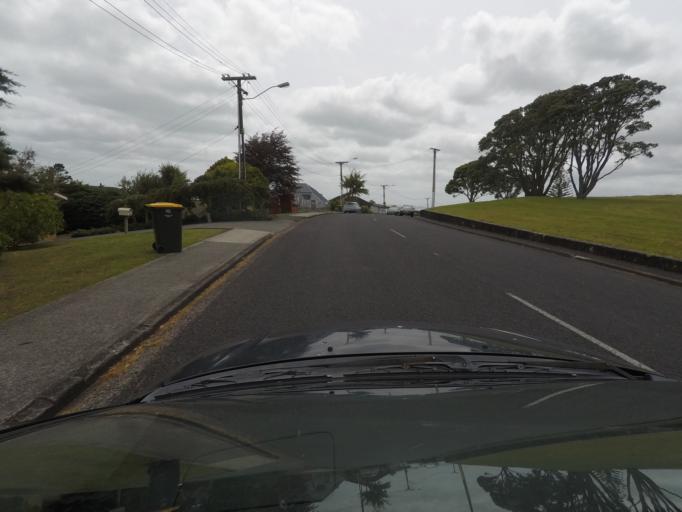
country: NZ
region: Auckland
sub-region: Auckland
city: Pakuranga
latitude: -36.8920
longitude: 174.9269
